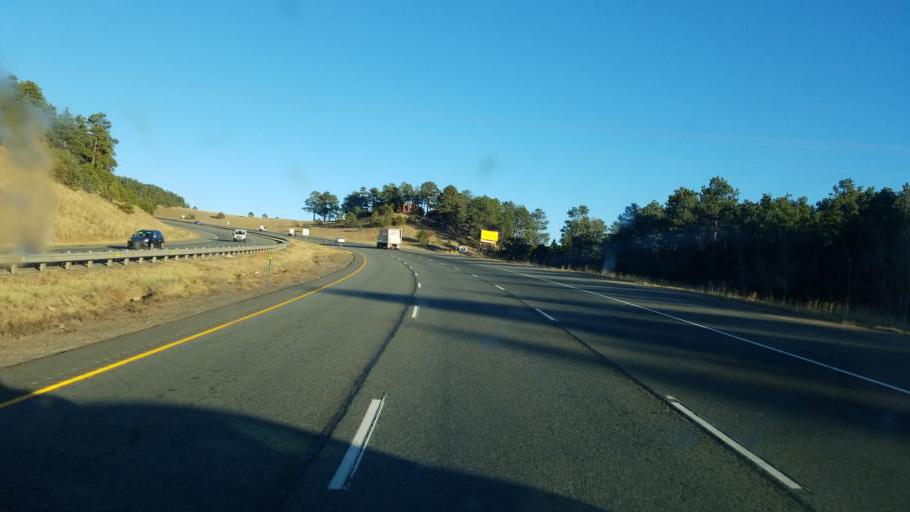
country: US
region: Colorado
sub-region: Jefferson County
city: Kittredge
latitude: 39.7016
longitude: -105.3349
